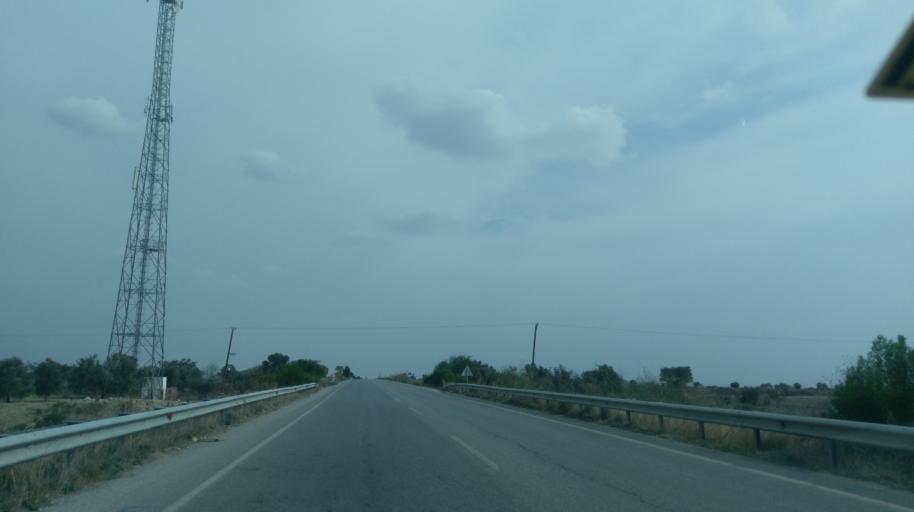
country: CY
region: Ammochostos
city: Lefkonoiko
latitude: 35.2598
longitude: 33.6622
